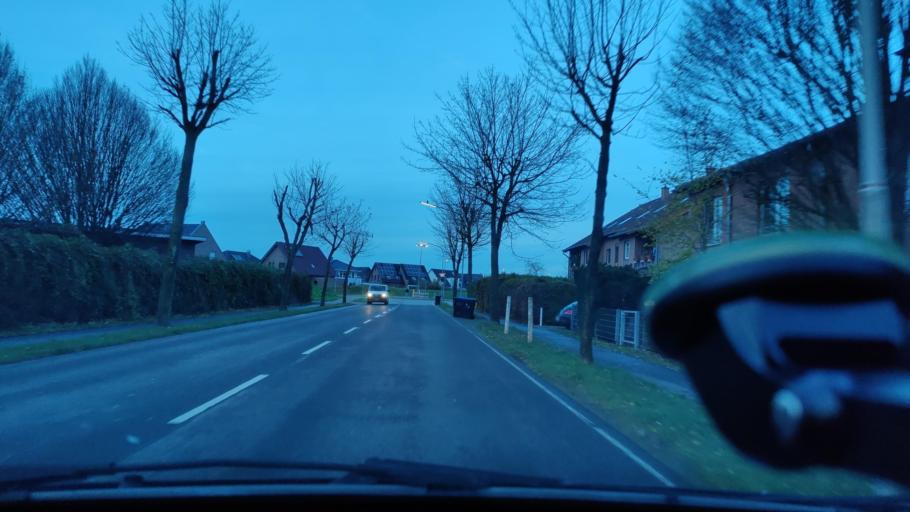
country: DE
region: North Rhine-Westphalia
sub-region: Regierungsbezirk Dusseldorf
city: Xanten
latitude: 51.6622
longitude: 6.4623
